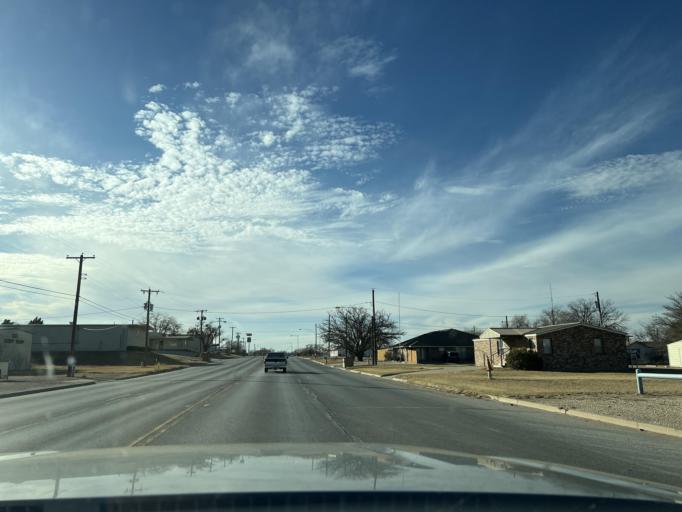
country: US
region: Texas
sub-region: Scurry County
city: Snyder
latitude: 32.7173
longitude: -100.9279
